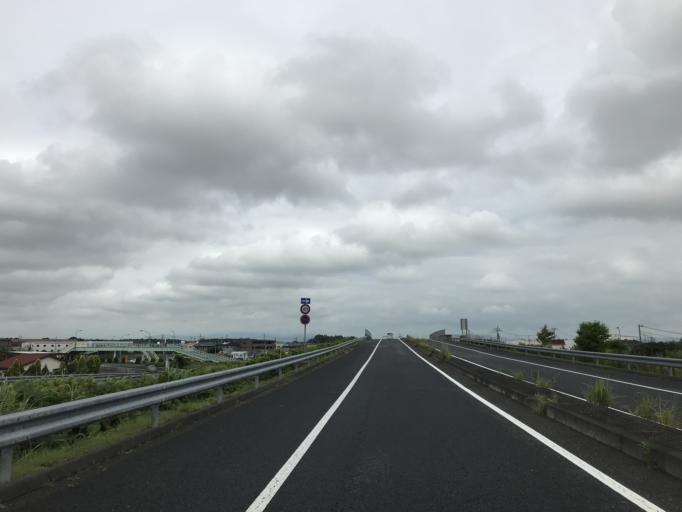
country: JP
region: Ibaraki
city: Mito-shi
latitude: 36.3166
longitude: 140.4538
